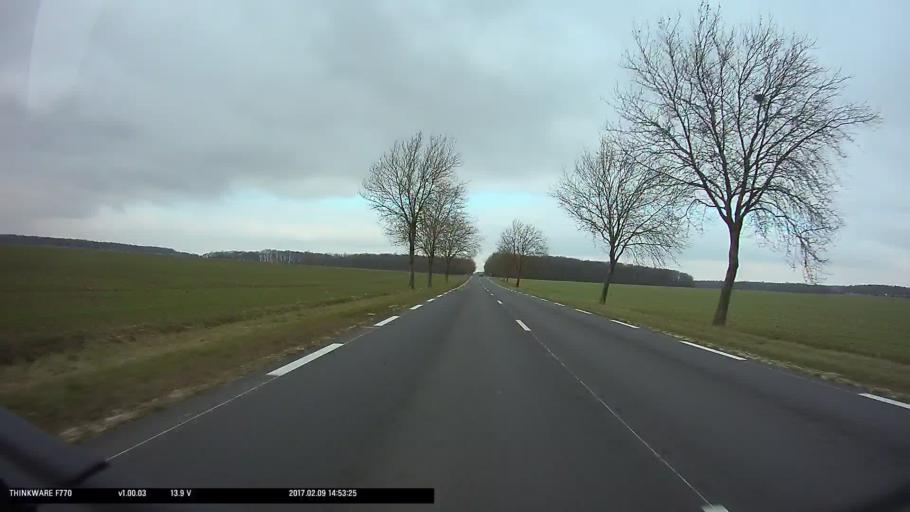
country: FR
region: Centre
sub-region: Departement du Cher
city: Levet
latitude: 46.9068
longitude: 2.4127
